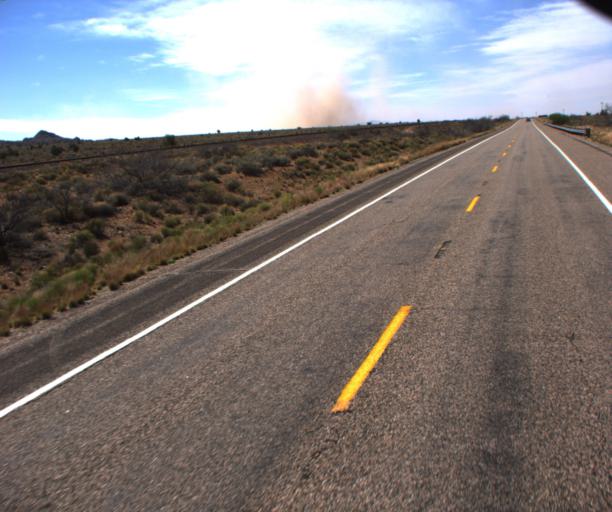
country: US
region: Arizona
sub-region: Mohave County
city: New Kingman-Butler
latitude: 35.4064
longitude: -113.7700
